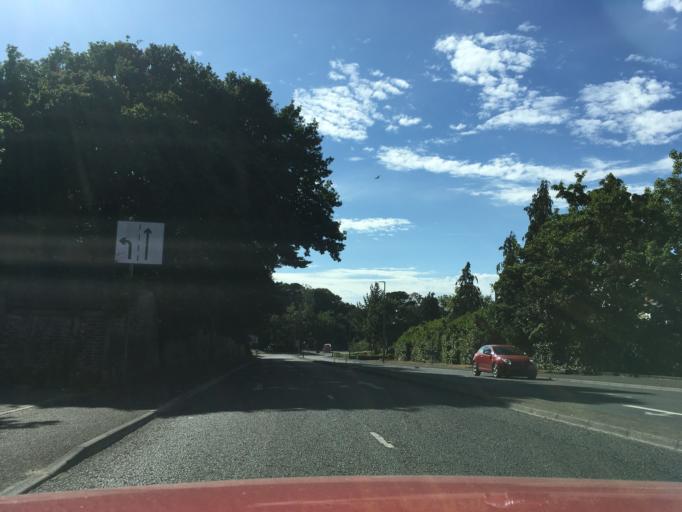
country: GB
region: England
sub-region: Bournemouth
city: Bournemouth
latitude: 50.7613
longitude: -1.8725
